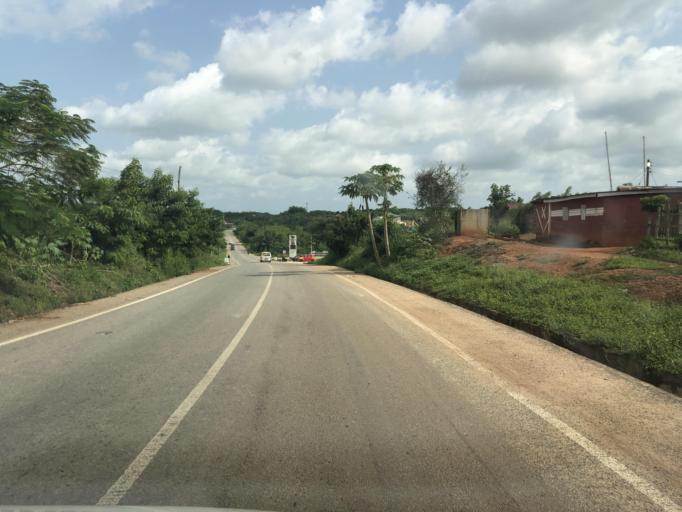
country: GH
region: Central
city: Elmina
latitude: 5.1942
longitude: -1.3192
